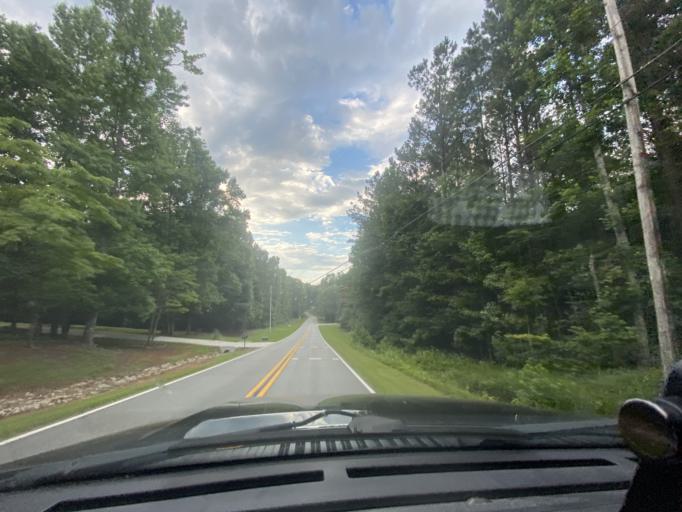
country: US
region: Georgia
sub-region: Fayette County
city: Peachtree City
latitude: 33.4173
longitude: -84.6650
